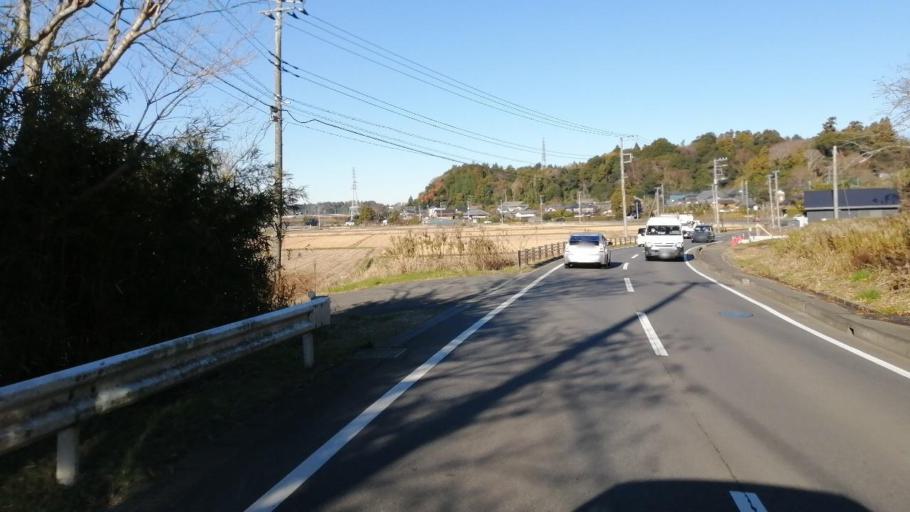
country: JP
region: Chiba
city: Narita
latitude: 35.7635
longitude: 140.3393
